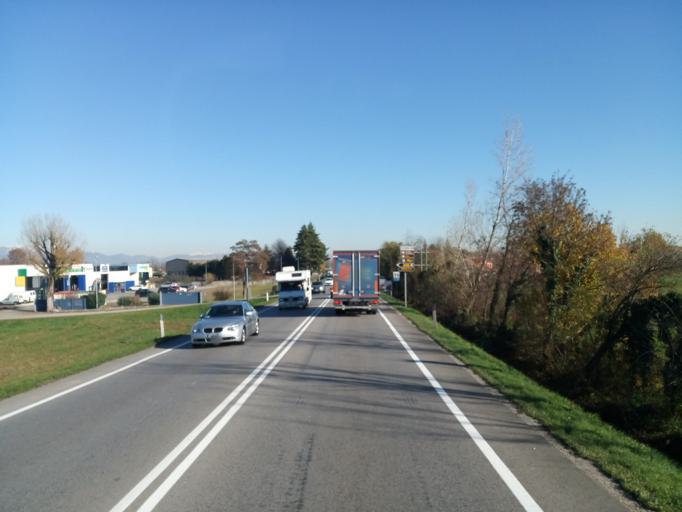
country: IT
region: Veneto
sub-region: Provincia di Treviso
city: Castelfranco Veneto
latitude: 45.6739
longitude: 11.9088
